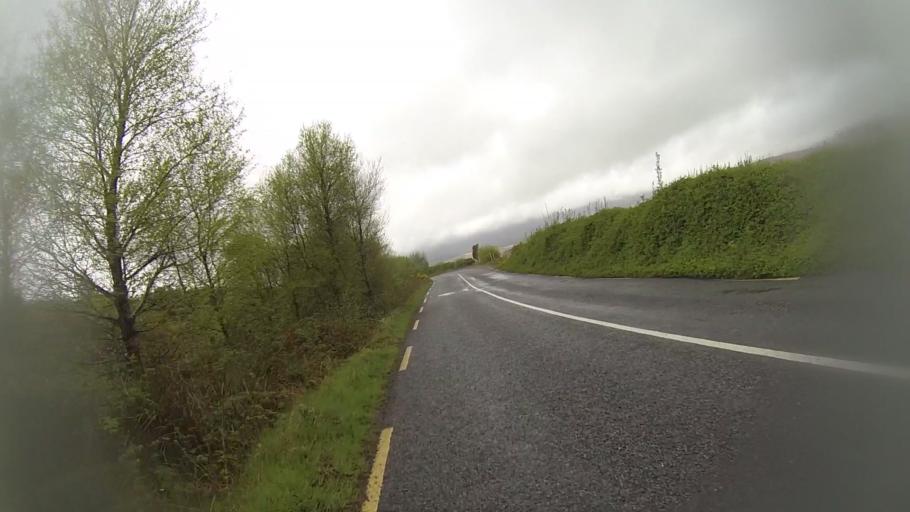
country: IE
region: Munster
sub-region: Ciarrai
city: Killorglin
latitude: 51.8552
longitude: -9.8705
